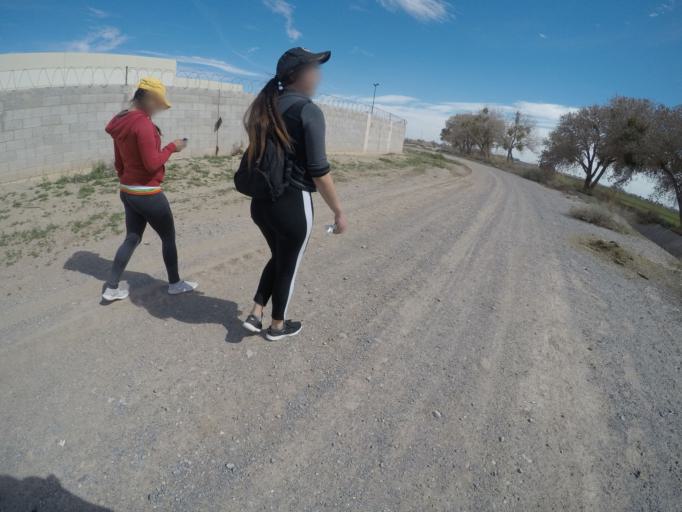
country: US
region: Texas
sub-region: El Paso County
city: Socorro
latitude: 31.6482
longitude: -106.3491
